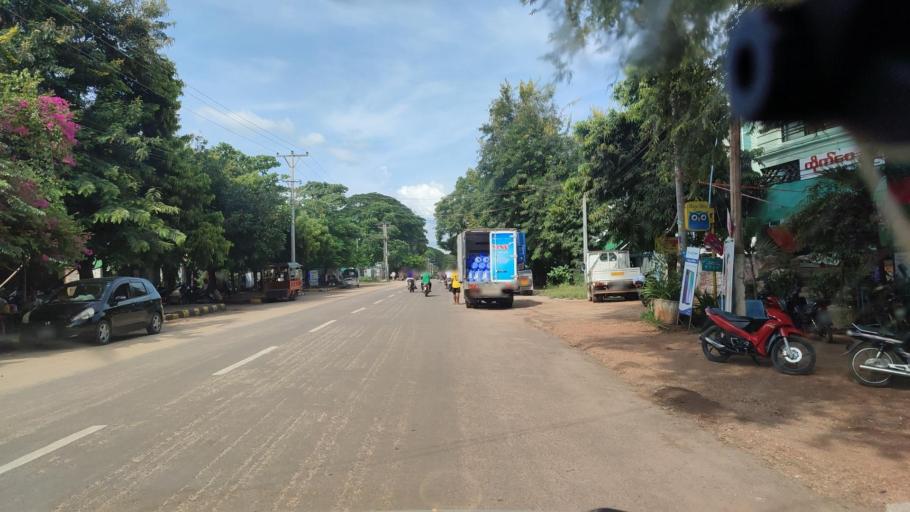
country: MM
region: Magway
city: Chauk
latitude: 20.8446
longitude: 95.1262
